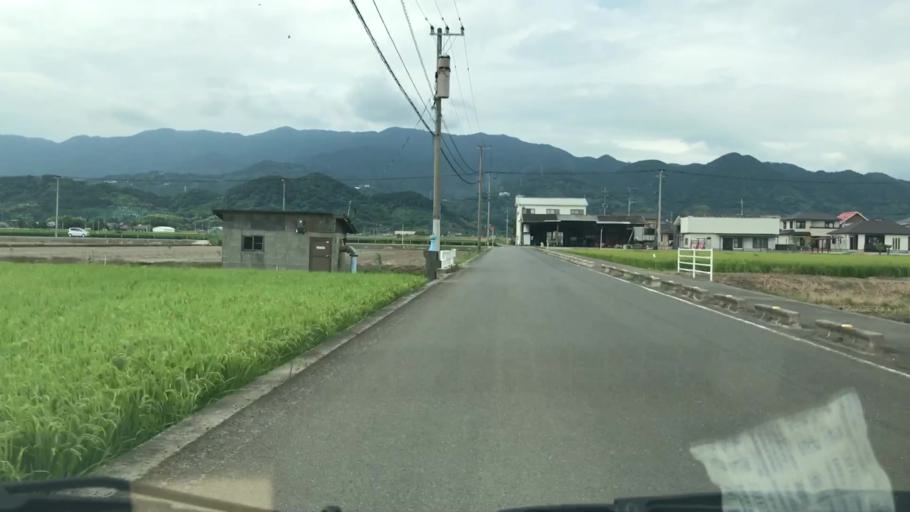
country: JP
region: Saga Prefecture
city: Saga-shi
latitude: 33.2879
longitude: 130.2248
